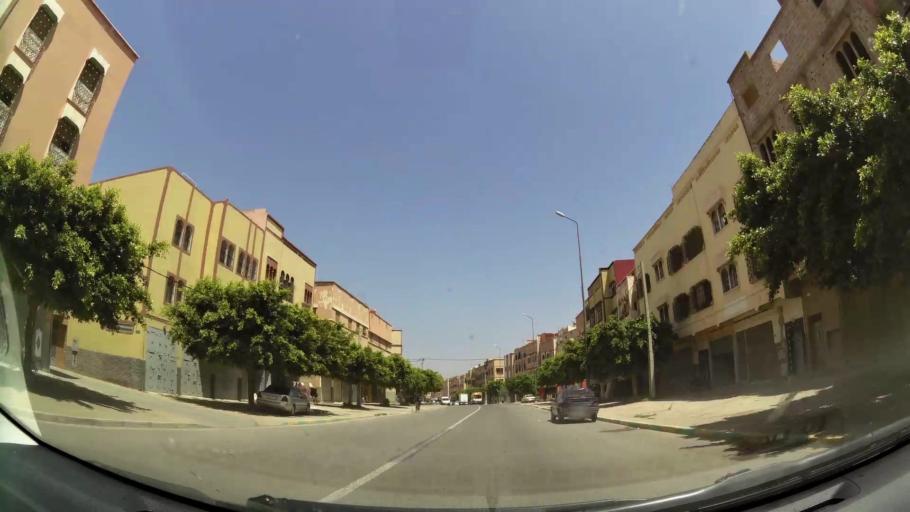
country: MA
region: Souss-Massa-Draa
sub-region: Inezgane-Ait Mellou
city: Inezgane
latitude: 30.3486
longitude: -9.4941
